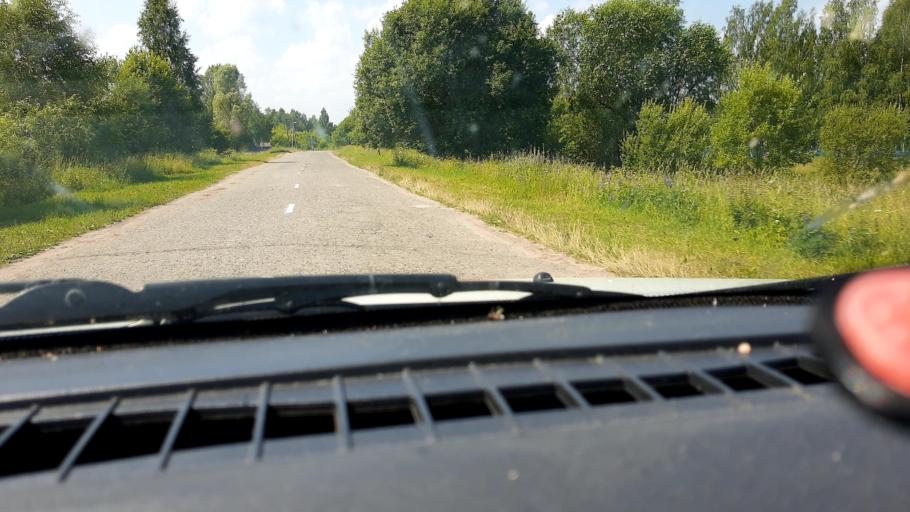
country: RU
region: Nizjnij Novgorod
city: Sharanga
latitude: 57.0525
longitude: 46.5539
